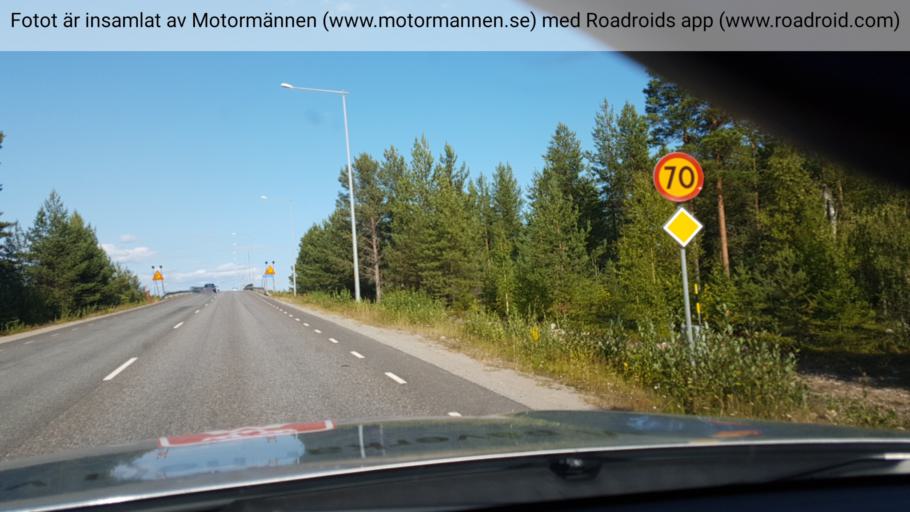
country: SE
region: Norrbotten
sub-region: Pitea Kommun
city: Pitea
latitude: 65.2293
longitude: 21.5109
